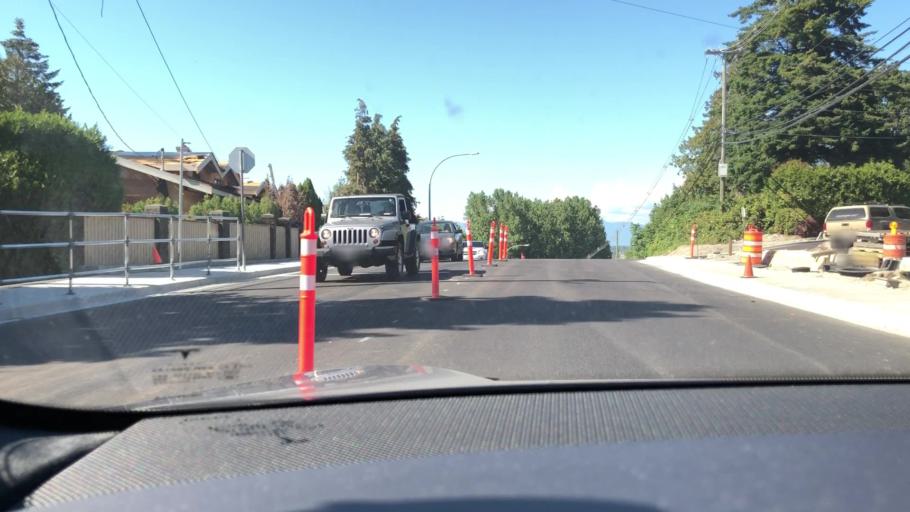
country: US
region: Washington
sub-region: Whatcom County
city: Point Roberts
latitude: 49.0283
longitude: -123.0798
